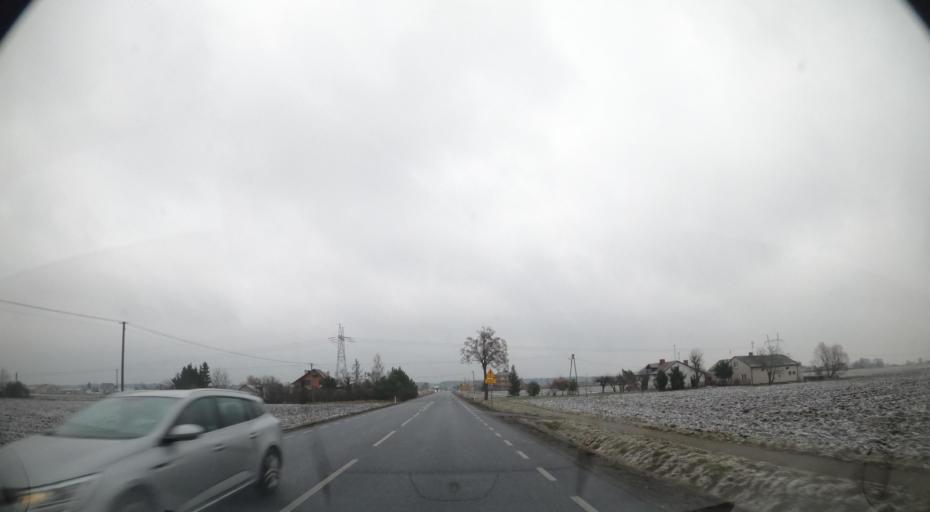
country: PL
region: Masovian Voivodeship
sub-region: Powiat sochaczewski
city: Mlodzieszyn
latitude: 52.2952
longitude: 20.1845
